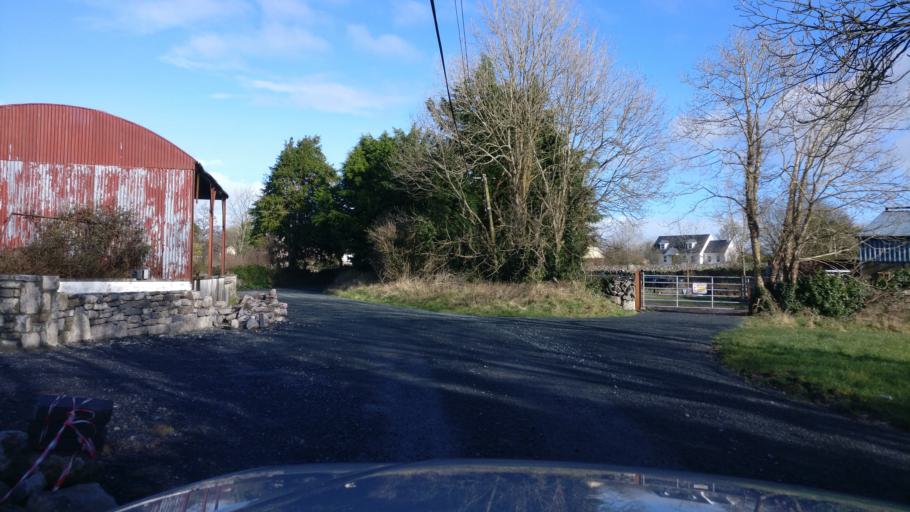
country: IE
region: Connaught
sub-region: County Galway
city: Athenry
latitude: 53.2319
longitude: -8.7757
